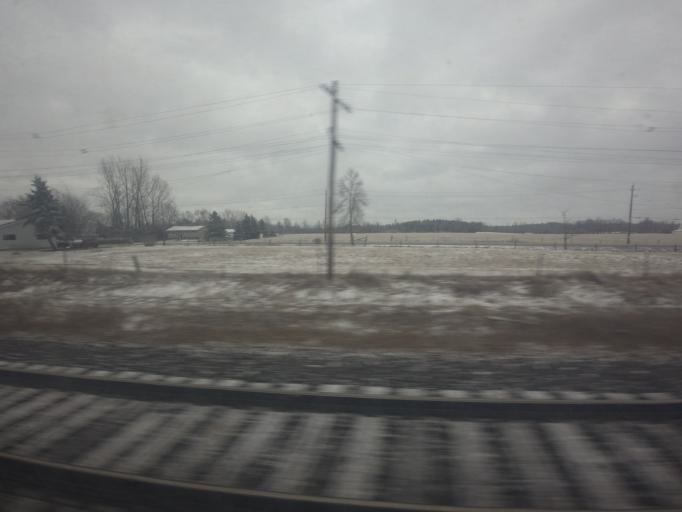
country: CA
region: Ontario
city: Gananoque
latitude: 44.3690
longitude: -76.1521
